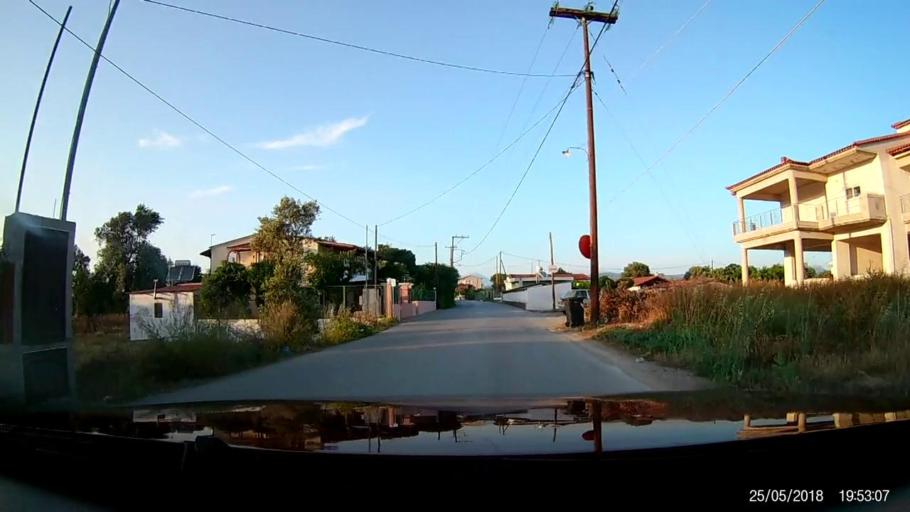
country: GR
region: Central Greece
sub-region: Nomos Evvoias
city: Ayios Nikolaos
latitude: 38.4151
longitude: 23.6491
